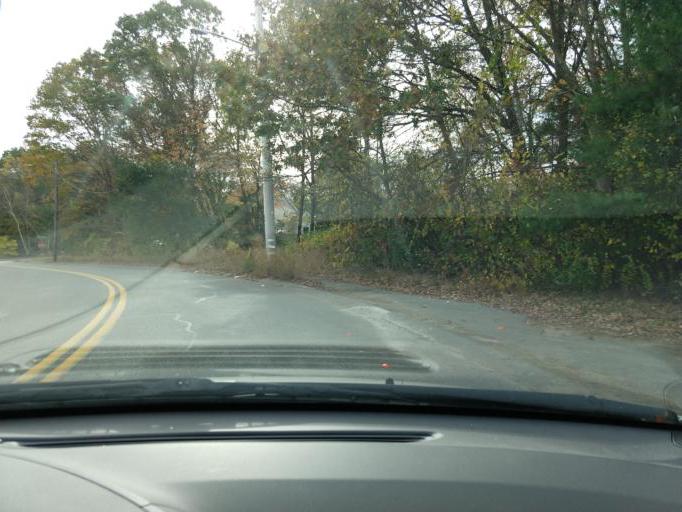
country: US
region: Massachusetts
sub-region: Middlesex County
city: Burlington
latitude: 42.5183
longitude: -71.1972
